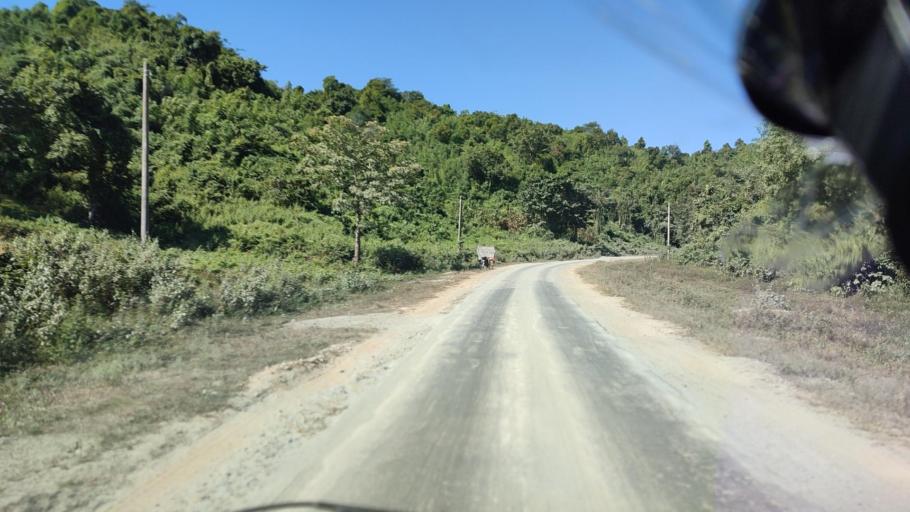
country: MM
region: Rakhine
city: Sittwe
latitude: 19.9477
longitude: 93.6590
